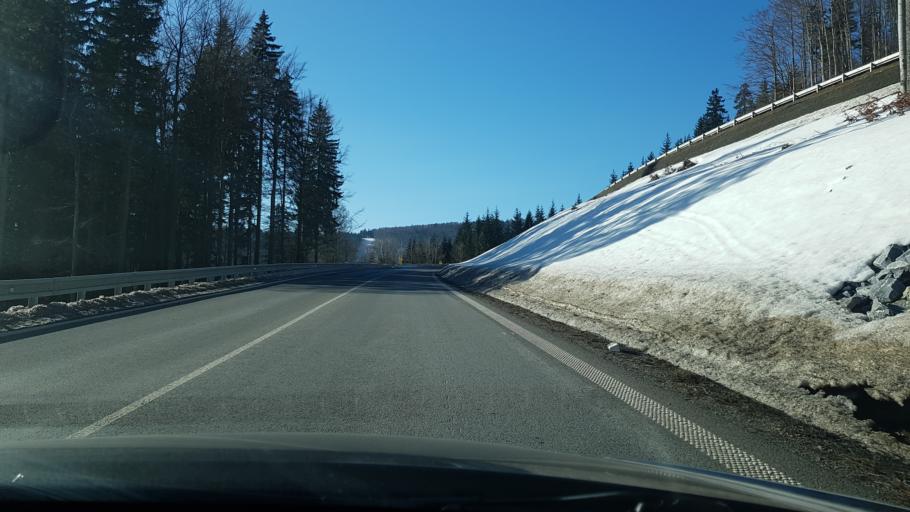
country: CZ
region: Olomoucky
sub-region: Okres Sumperk
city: Loucna nad Desnou
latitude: 50.1140
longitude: 17.1477
